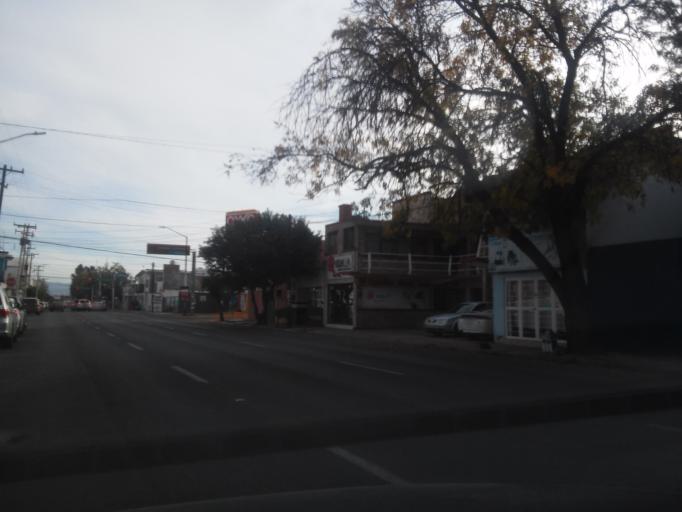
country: MX
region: Durango
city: Victoria de Durango
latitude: 24.0305
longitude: -104.6566
